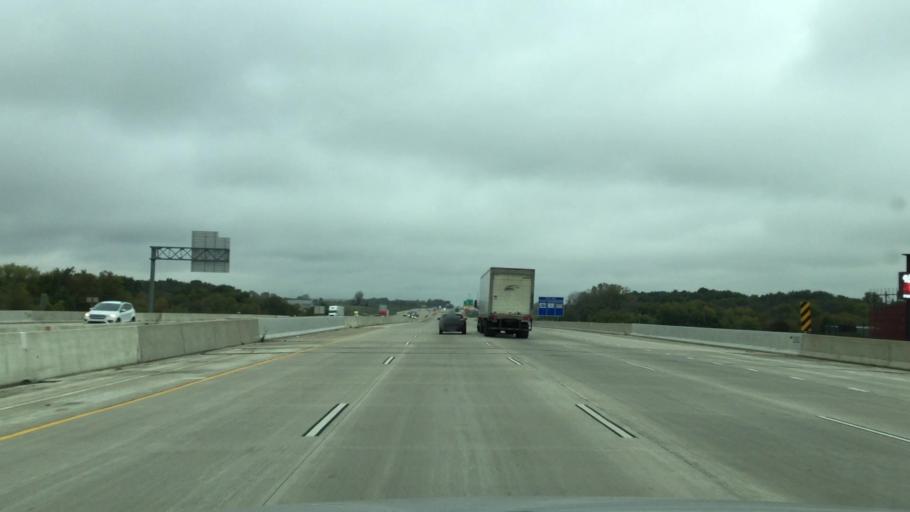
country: US
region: Wisconsin
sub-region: Kenosha County
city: Pleasant Prairie
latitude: 42.5817
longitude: -87.9529
